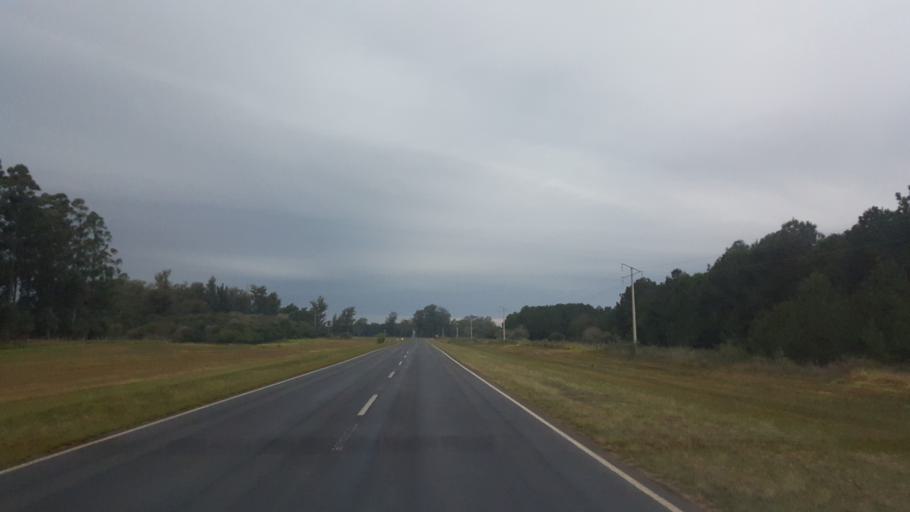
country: AR
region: Corrientes
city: Ituzaingo
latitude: -27.6125
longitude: -56.4309
